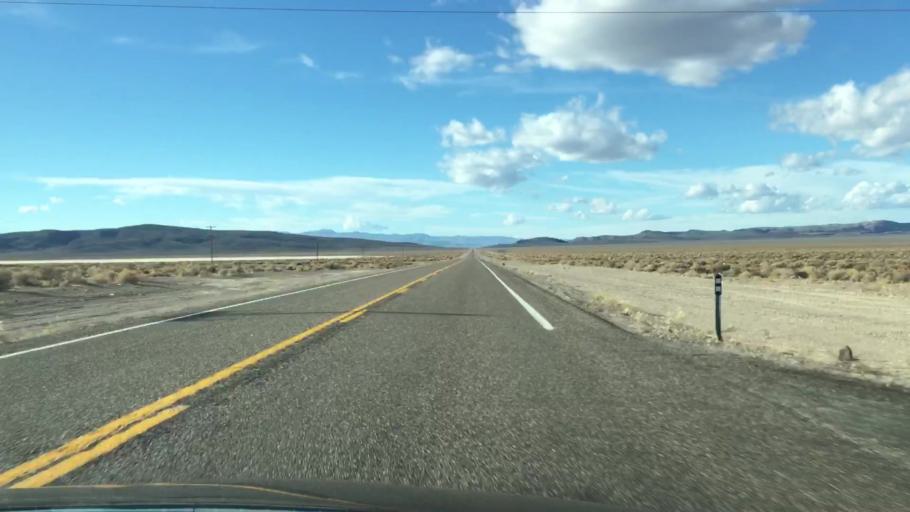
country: US
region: Nevada
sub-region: Nye County
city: Beatty
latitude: 37.1383
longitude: -116.8555
